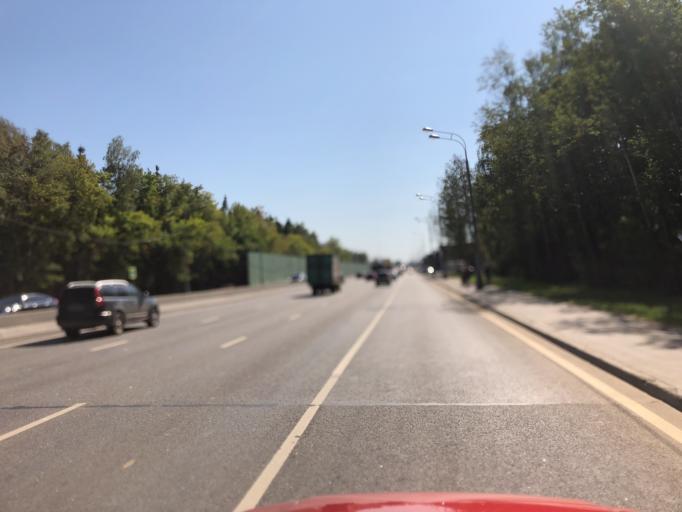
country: RU
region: Moskovskaya
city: Troitsk
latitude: 55.4616
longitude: 37.2981
